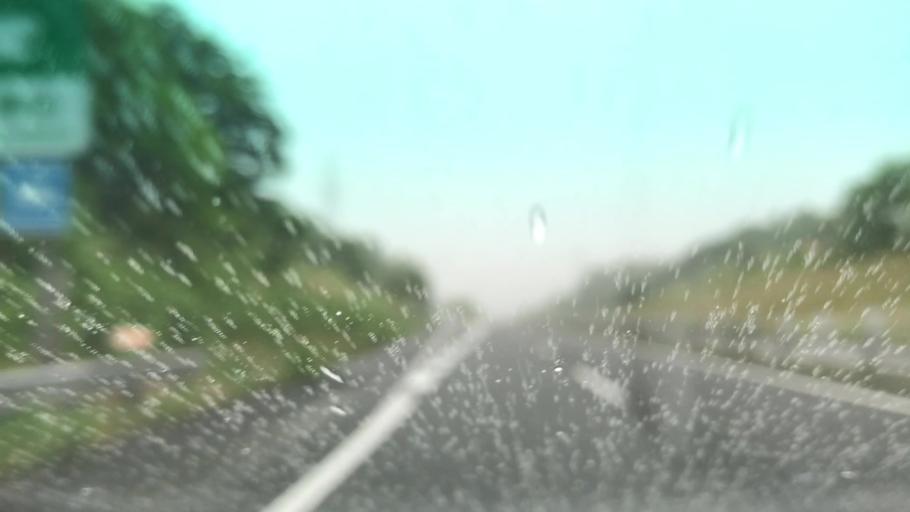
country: JP
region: Hokkaido
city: Shiraoi
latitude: 42.6141
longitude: 141.4683
